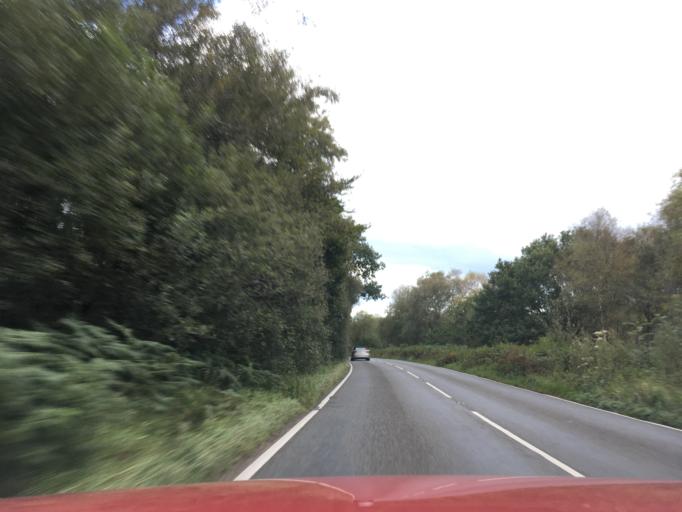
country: GB
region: England
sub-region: Devon
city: Honiton
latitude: 50.7780
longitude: -3.2066
